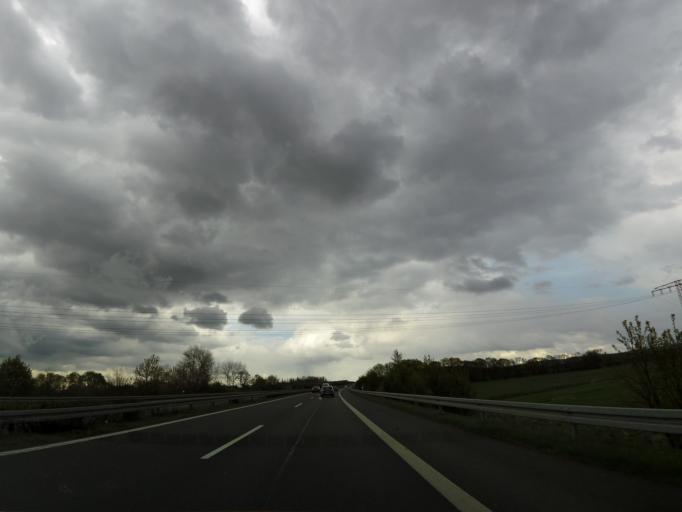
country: DE
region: Saxony-Anhalt
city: Veckenstedt
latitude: 51.8794
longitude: 10.7363
